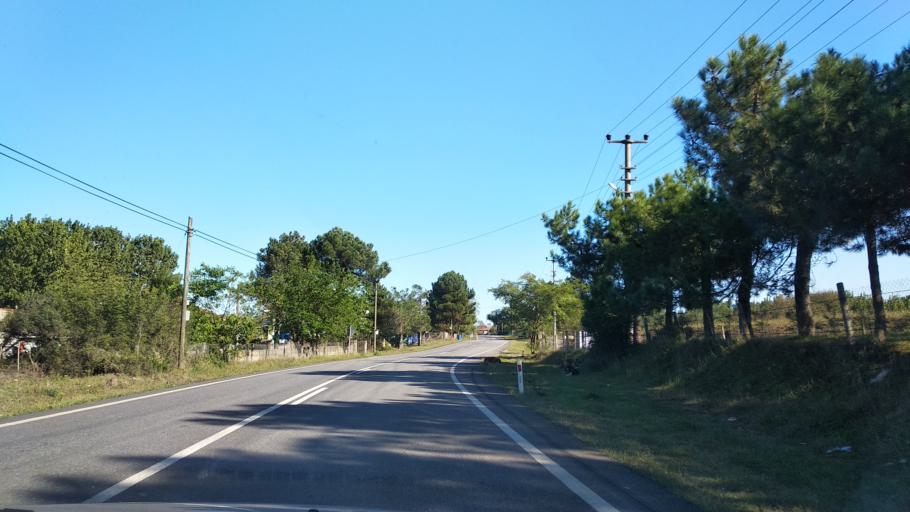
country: TR
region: Sakarya
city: Karasu
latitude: 41.1186
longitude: 30.6161
